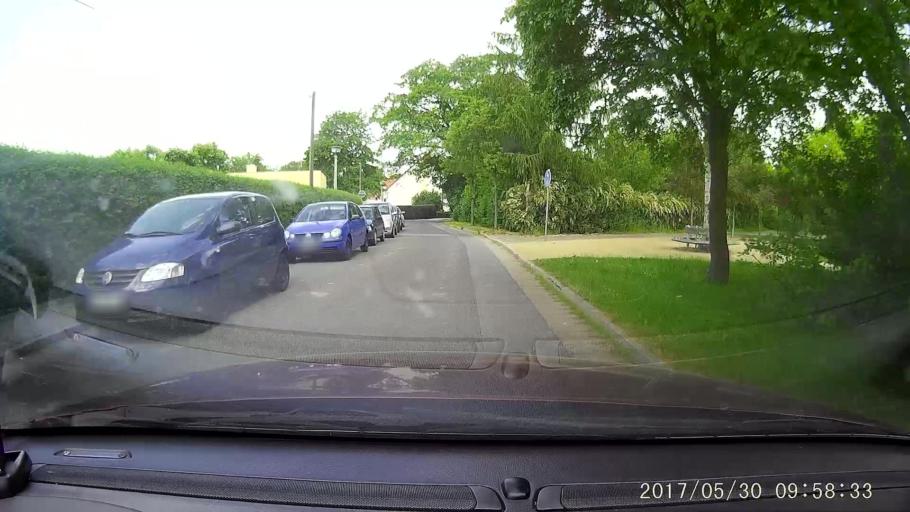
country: DE
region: Saxony
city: Goerlitz
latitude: 51.1411
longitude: 14.9421
